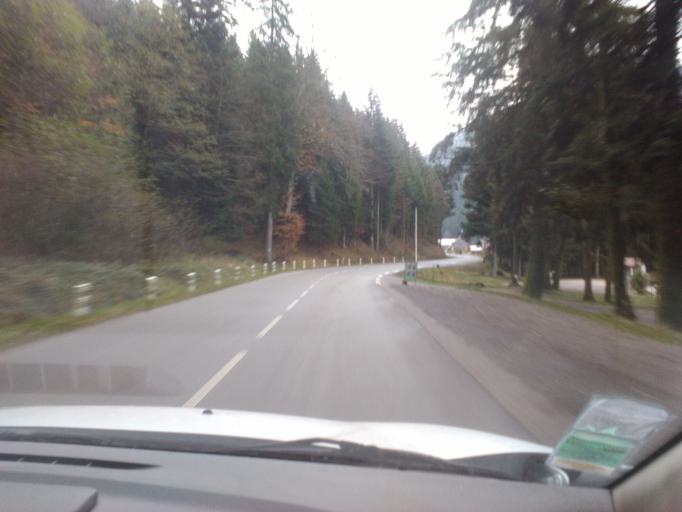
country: FR
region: Lorraine
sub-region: Departement des Vosges
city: Xonrupt-Longemer
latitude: 48.0670
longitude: 6.9589
